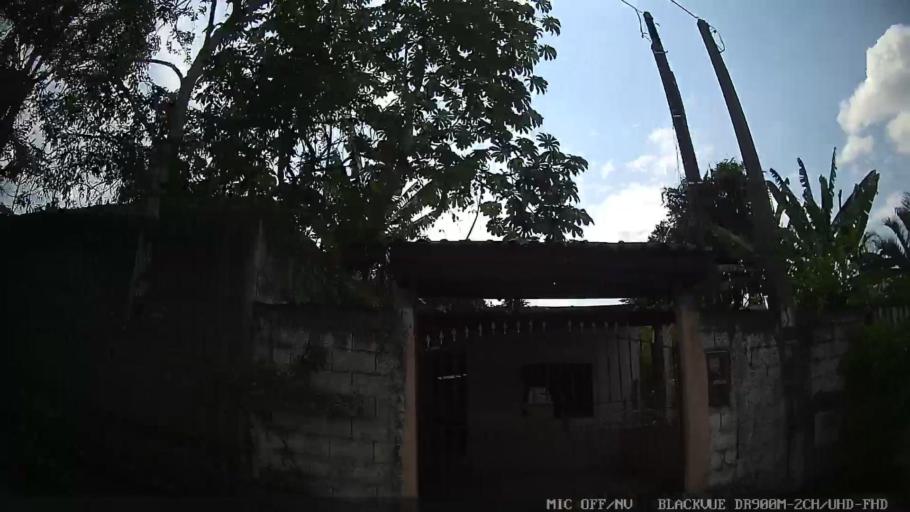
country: BR
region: Sao Paulo
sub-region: Caraguatatuba
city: Caraguatatuba
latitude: -23.6737
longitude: -45.4494
